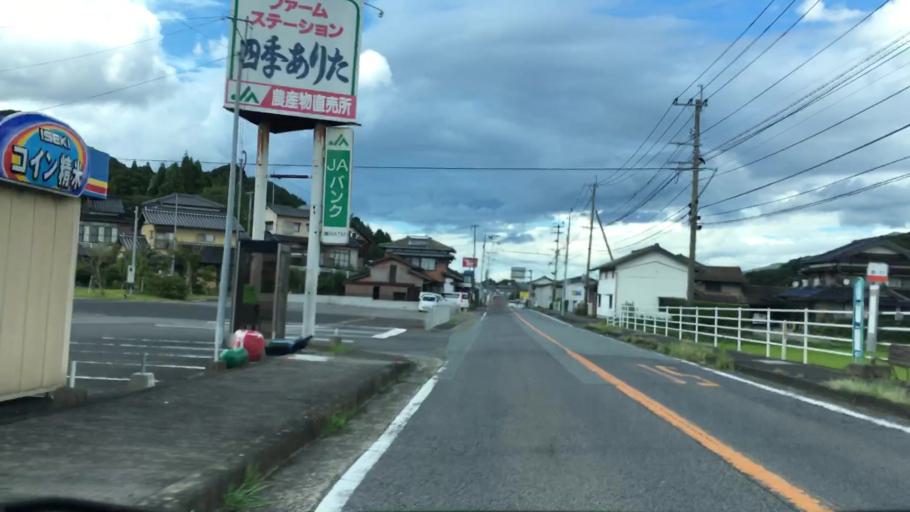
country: JP
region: Saga Prefecture
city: Imaricho-ko
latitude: 33.1966
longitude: 129.8506
